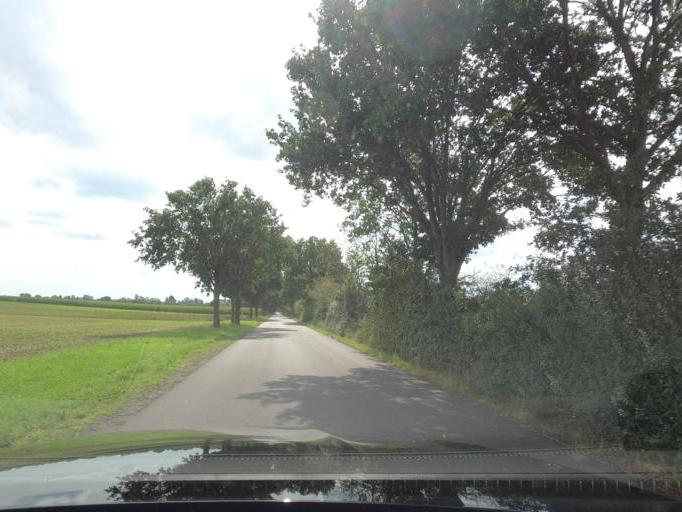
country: DE
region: Lower Saxony
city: Isernhagen Farster Bauerschaft
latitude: 52.5204
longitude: 9.8708
